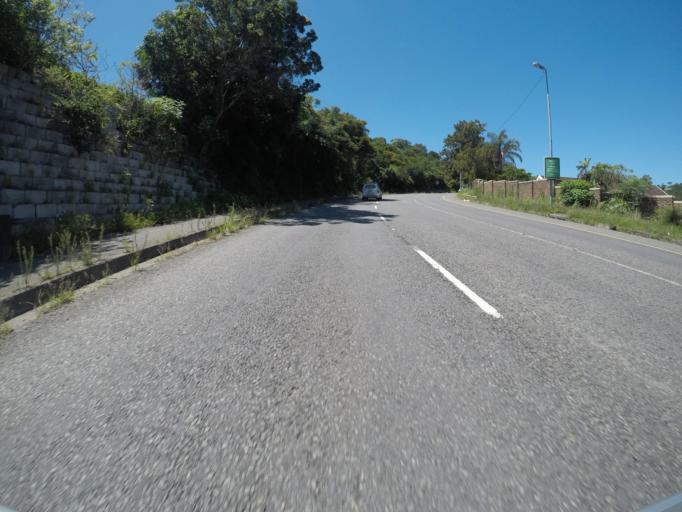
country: ZA
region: Eastern Cape
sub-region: Buffalo City Metropolitan Municipality
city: East London
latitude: -32.9710
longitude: 27.9288
